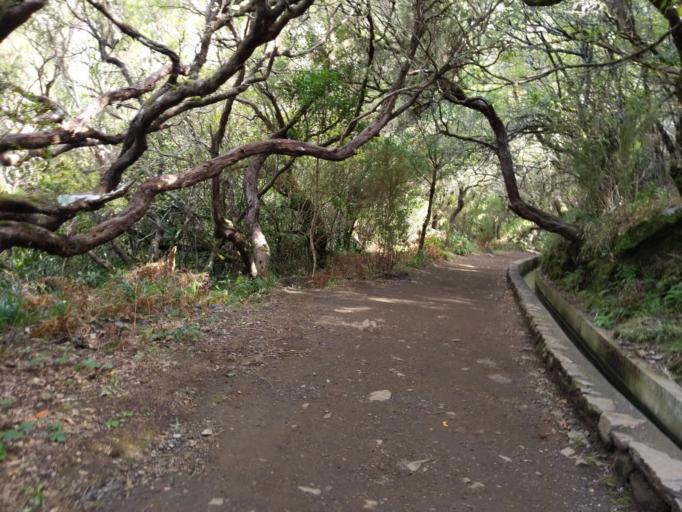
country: PT
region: Madeira
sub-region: Calheta
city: Arco da Calheta
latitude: 32.7626
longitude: -17.1286
